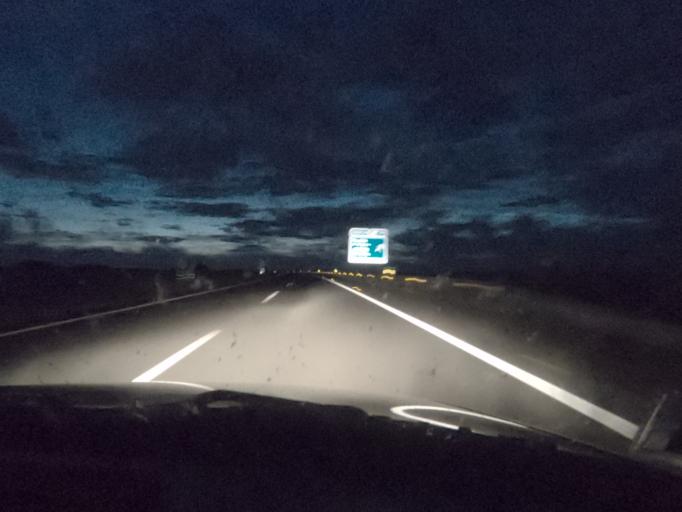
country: ES
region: Extremadura
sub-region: Provincia de Caceres
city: Morcillo
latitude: 39.9881
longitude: -6.4332
